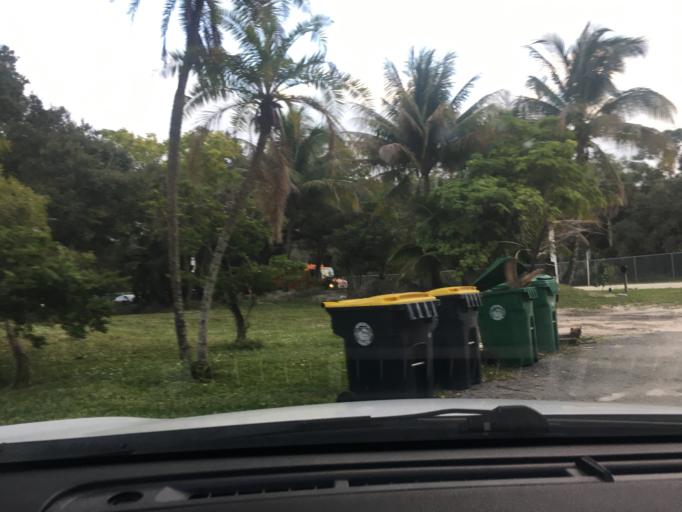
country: US
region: Florida
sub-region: Broward County
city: Dania Beach
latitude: 26.0704
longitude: -80.1708
